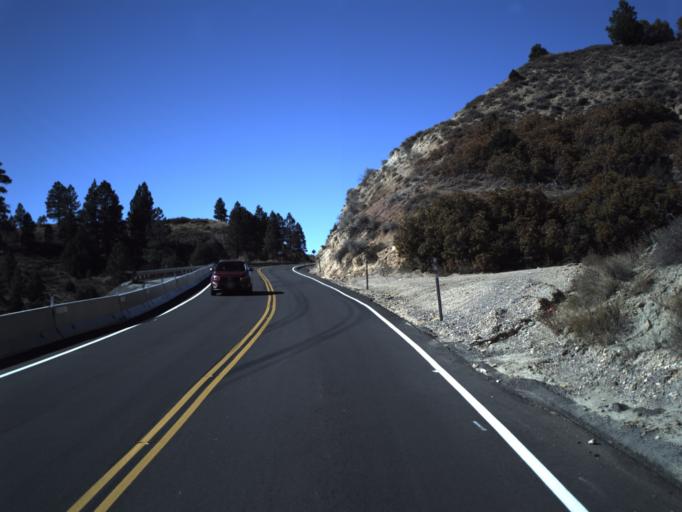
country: US
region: Utah
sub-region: Garfield County
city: Panguitch
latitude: 37.6839
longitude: -112.1321
